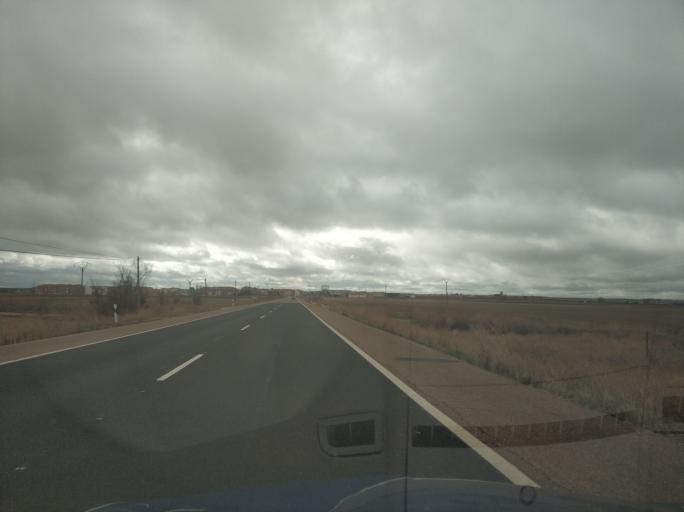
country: ES
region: Castille and Leon
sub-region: Provincia de Salamanca
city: Castellanos de Moriscos
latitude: 41.0264
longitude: -5.5852
